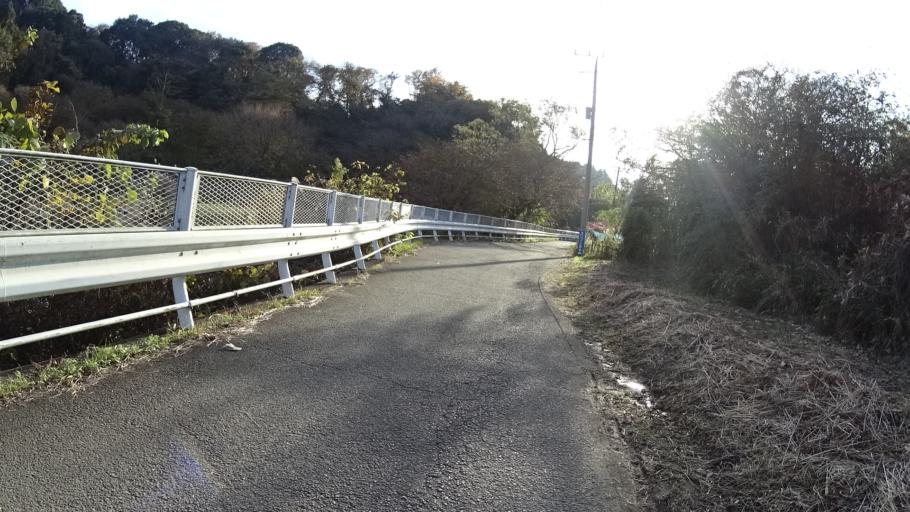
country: JP
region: Kanagawa
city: Kamakura
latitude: 35.3646
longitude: 139.5773
